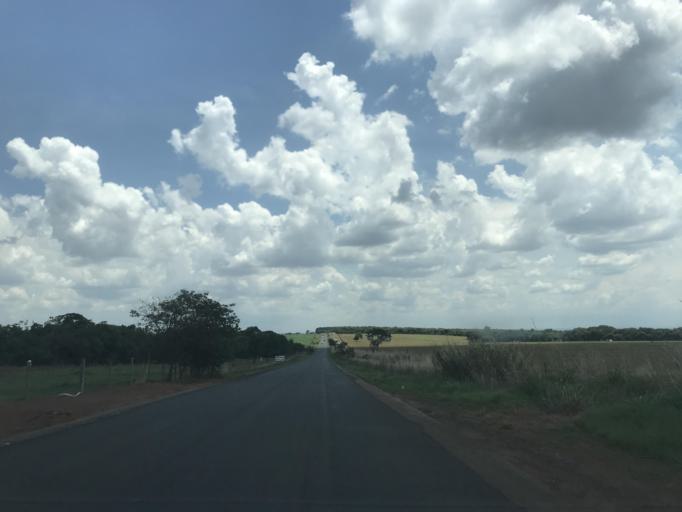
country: BR
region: Goias
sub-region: Piracanjuba
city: Piracanjuba
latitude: -17.3492
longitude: -48.7938
